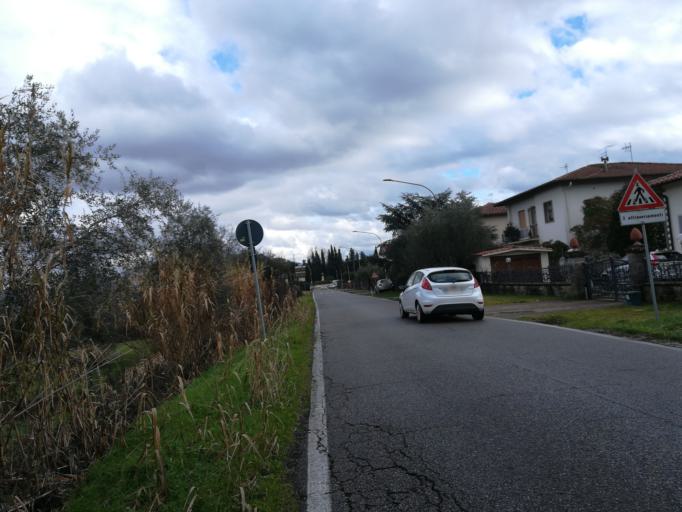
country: IT
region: Tuscany
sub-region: Provincia di Prato
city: Poggio A Caiano
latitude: 43.8083
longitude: 11.0430
